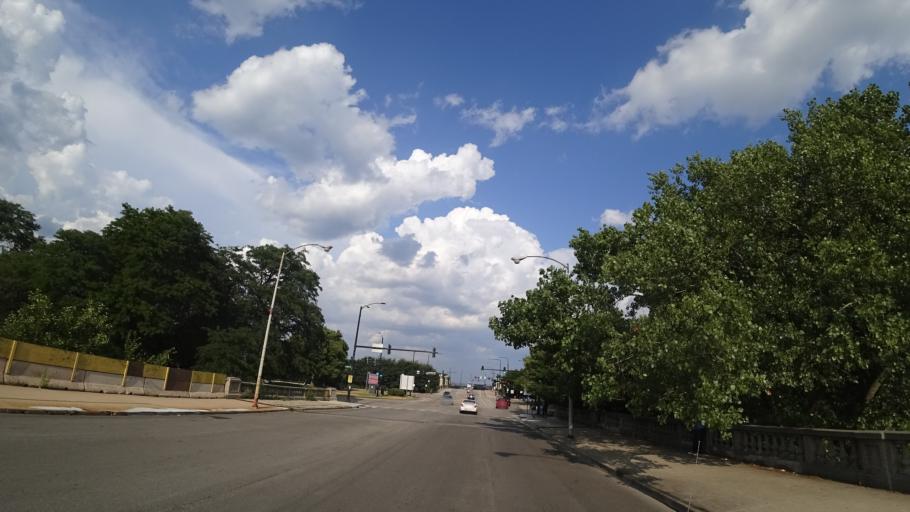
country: US
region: Illinois
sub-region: Cook County
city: Chicago
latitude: 41.8385
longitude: -87.6105
